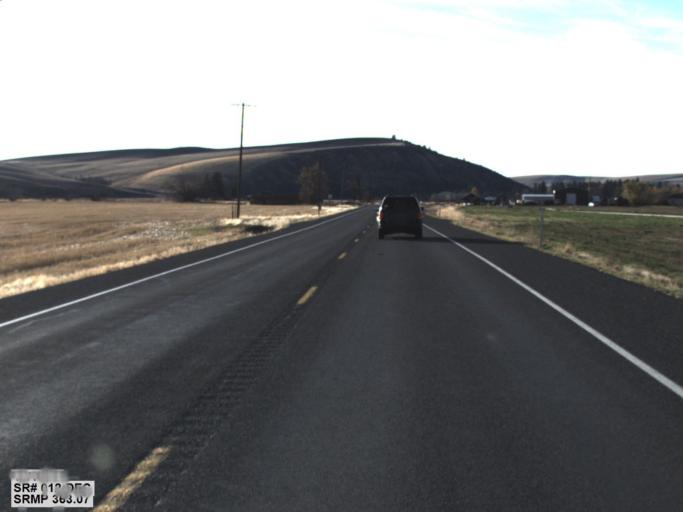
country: US
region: Washington
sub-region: Columbia County
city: Dayton
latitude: 46.2876
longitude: -118.0489
